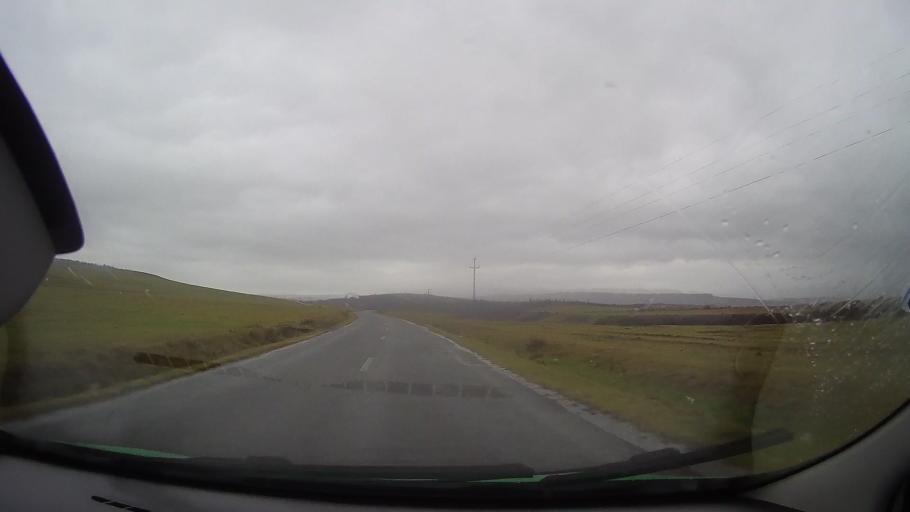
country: RO
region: Mures
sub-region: Comuna Brancovenesti
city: Valenii de Mures
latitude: 46.9066
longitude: 24.7844
